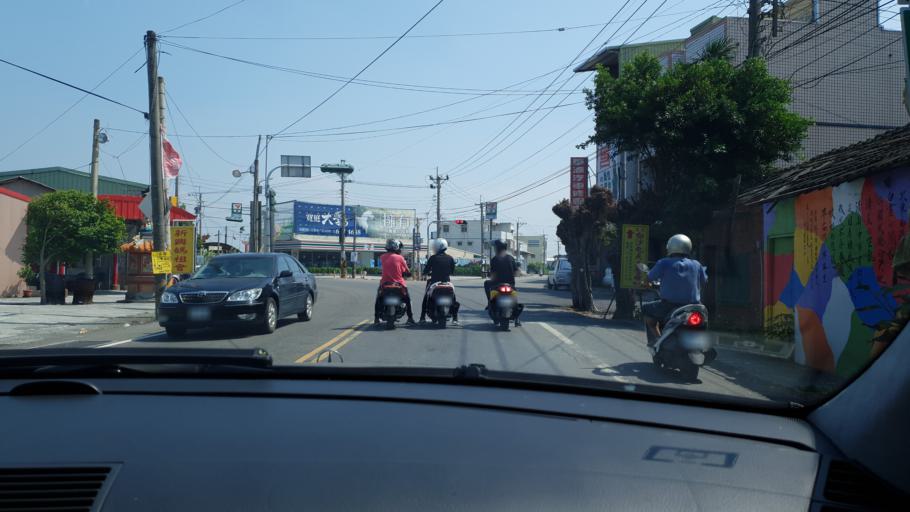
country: TW
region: Taiwan
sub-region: Yunlin
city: Douliu
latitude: 23.7400
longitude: 120.4252
